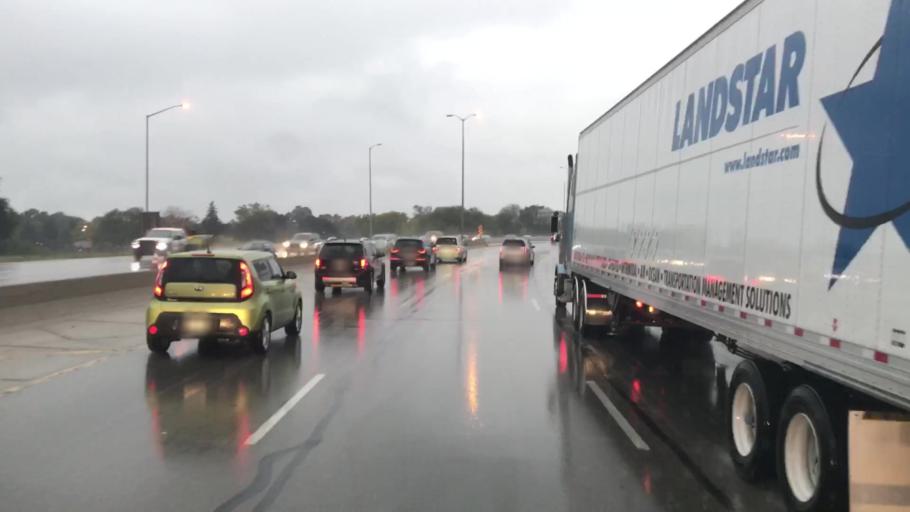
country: US
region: Wisconsin
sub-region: Waukesha County
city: Elm Grove
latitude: 43.0588
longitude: -88.0528
